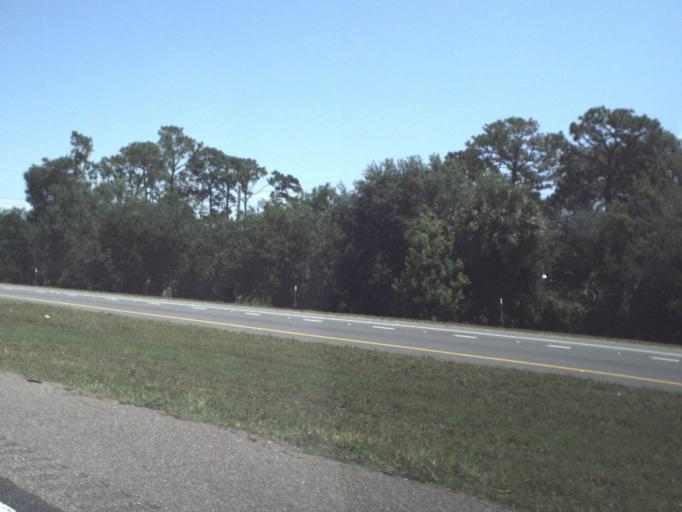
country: US
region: Florida
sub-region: Duval County
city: Jacksonville
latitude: 30.4157
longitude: -81.5649
